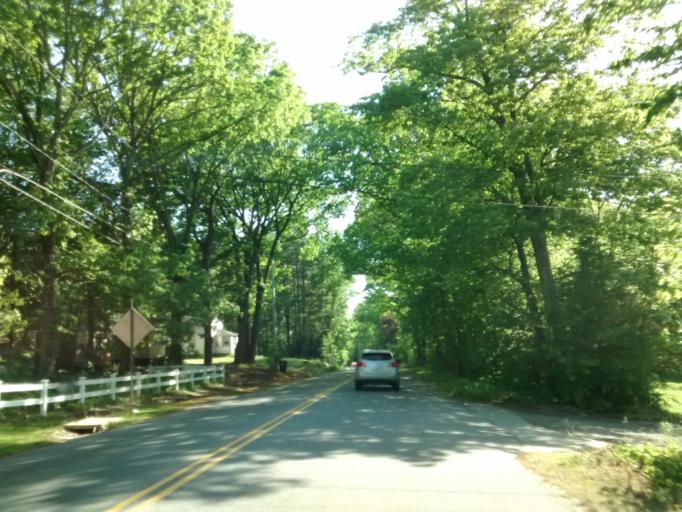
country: US
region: Massachusetts
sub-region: Worcester County
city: Charlton
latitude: 42.1512
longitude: -71.9824
